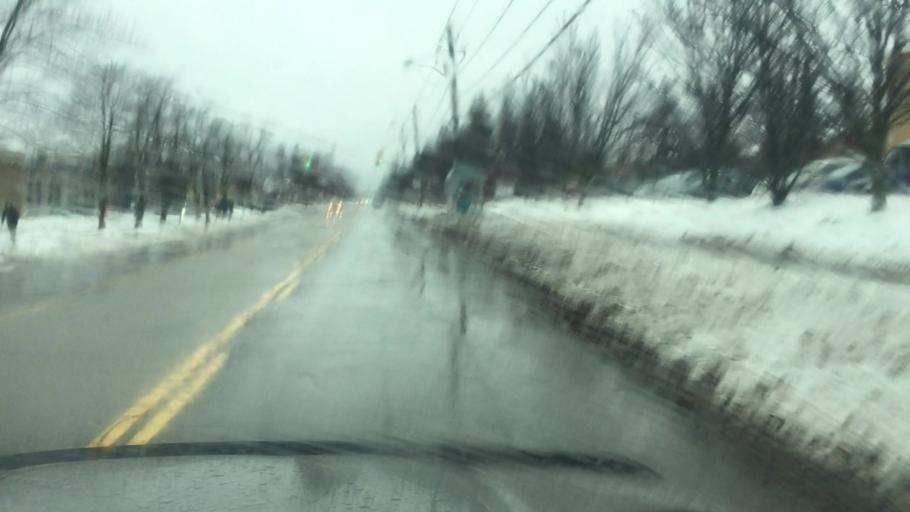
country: CA
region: Ontario
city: Ajax
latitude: 43.8571
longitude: -79.0567
